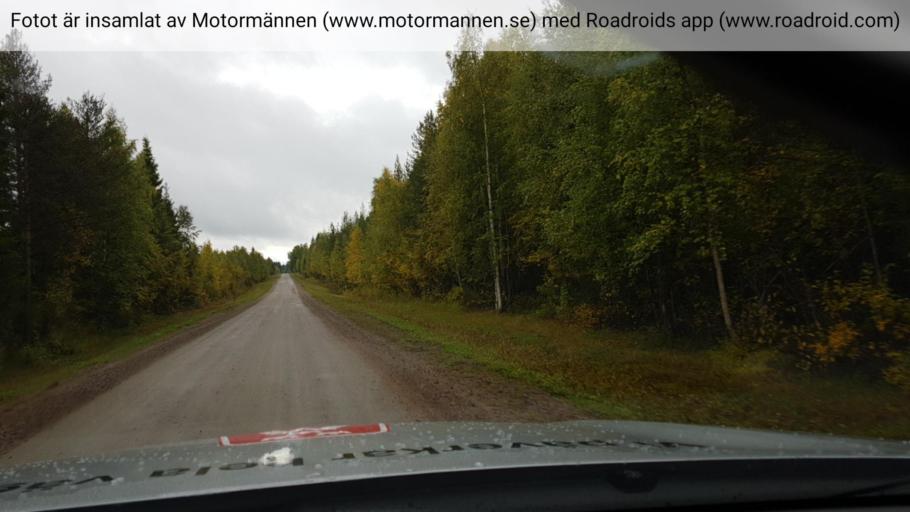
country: SE
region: Norrbotten
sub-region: Alvsbyns Kommun
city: AElvsbyn
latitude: 66.1948
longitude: 20.8437
